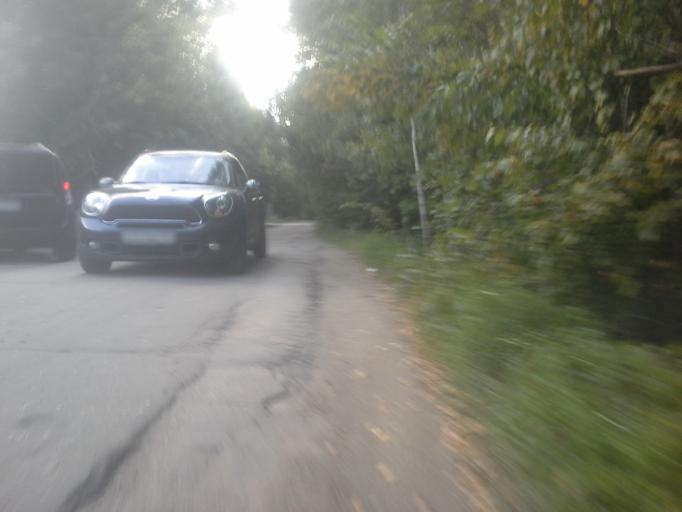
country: RU
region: Moskovskaya
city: Selyatino
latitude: 55.4956
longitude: 36.9859
